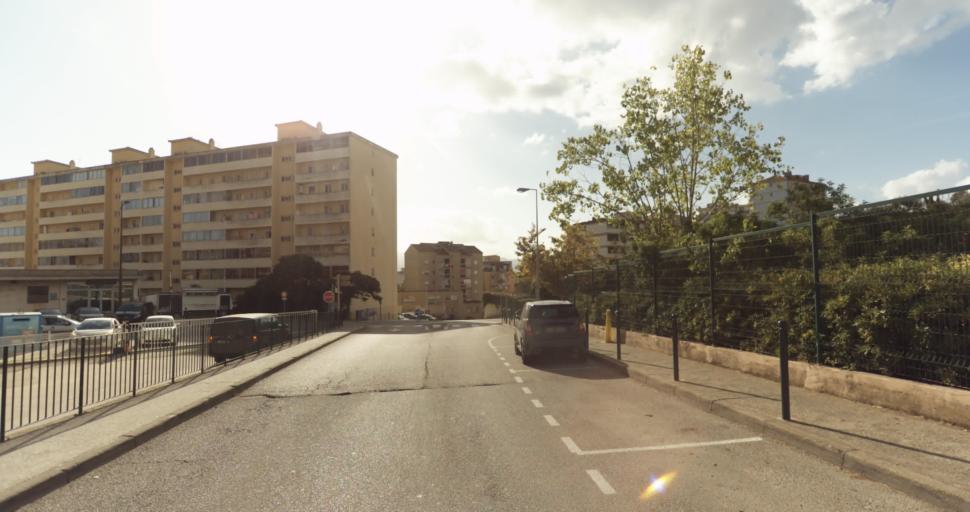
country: FR
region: Corsica
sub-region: Departement de la Corse-du-Sud
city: Ajaccio
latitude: 41.9299
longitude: 8.7329
